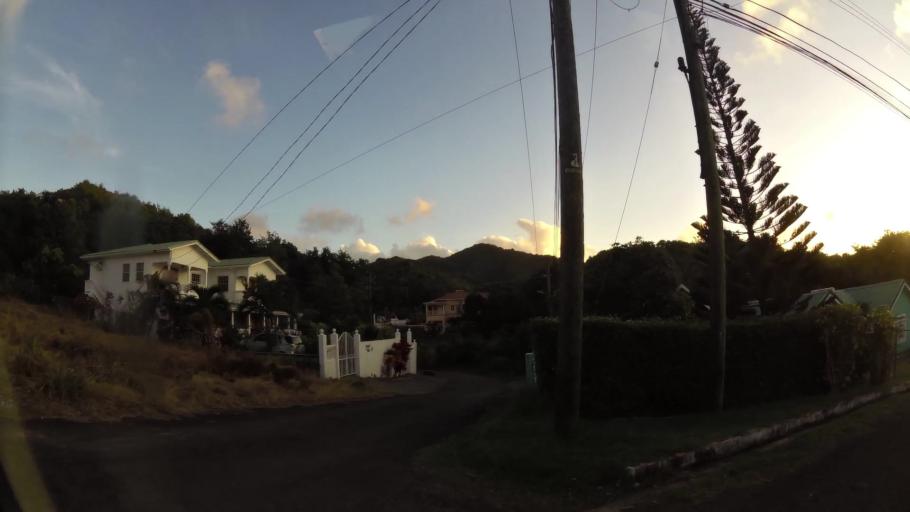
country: LC
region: Gros-Islet
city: Gros Islet
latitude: 14.0652
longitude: -60.9533
